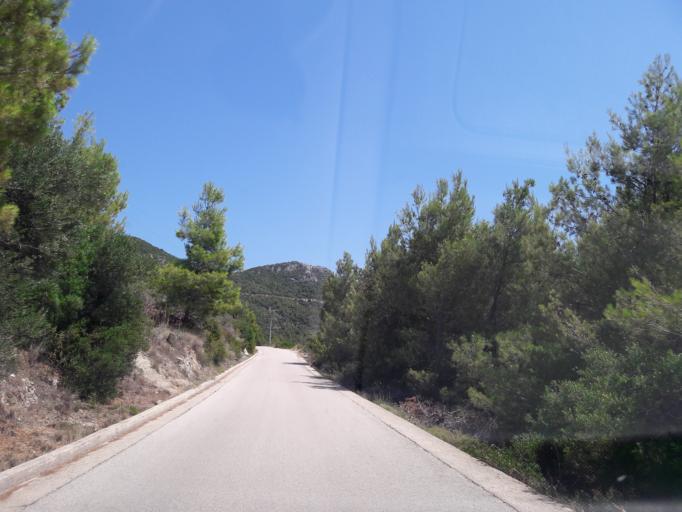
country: HR
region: Dubrovacko-Neretvanska
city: Blato
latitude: 42.9134
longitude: 17.4143
